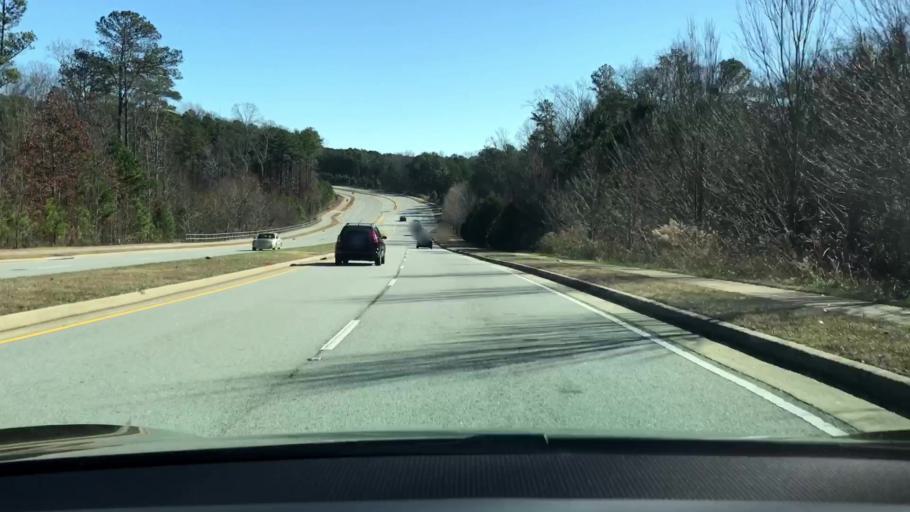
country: US
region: Georgia
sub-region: Gwinnett County
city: Suwanee
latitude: 34.0222
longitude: -84.0506
